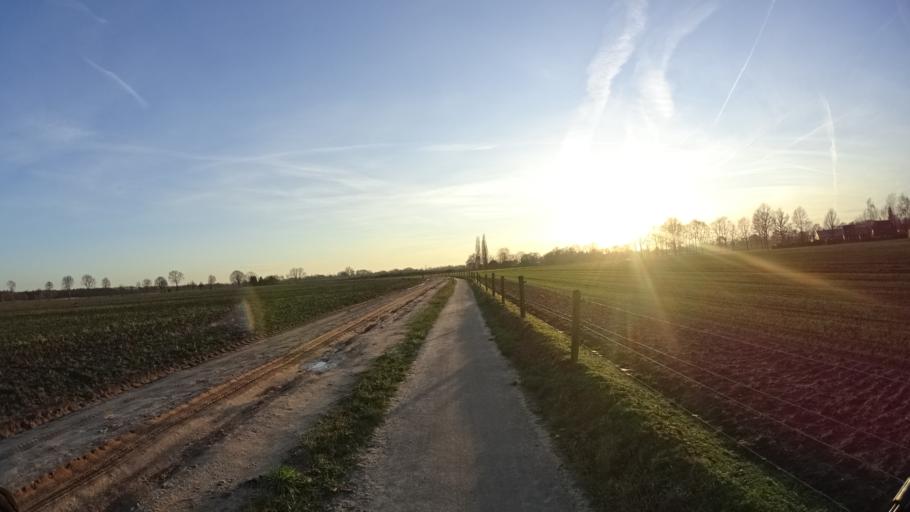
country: NL
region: Gelderland
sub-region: Gemeente Ede
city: Lunteren
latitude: 52.0731
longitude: 5.6442
